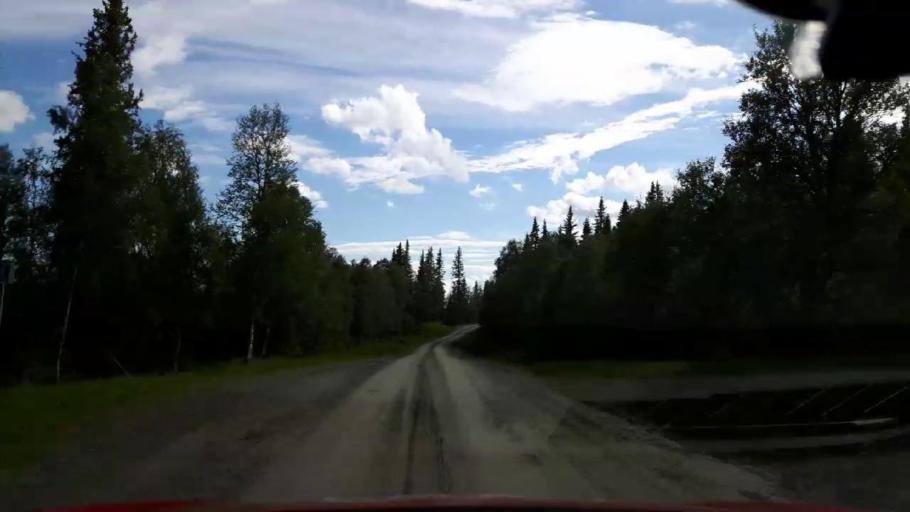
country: SE
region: Jaemtland
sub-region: Krokoms Kommun
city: Valla
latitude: 63.8576
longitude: 14.0972
